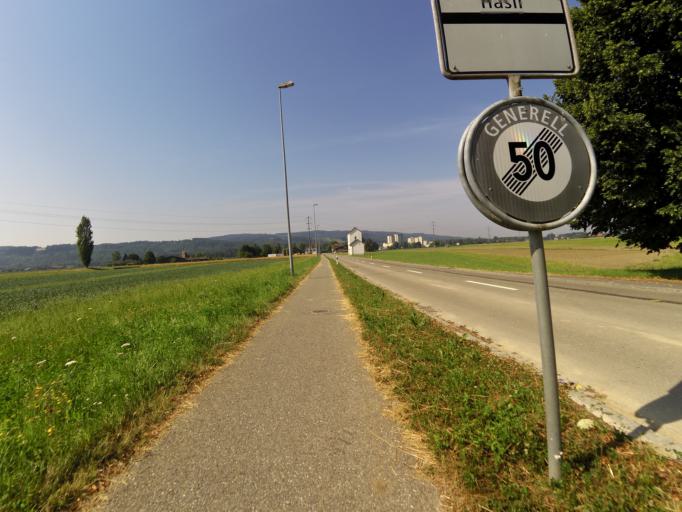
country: CH
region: Thurgau
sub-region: Weinfelden District
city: Wigoltingen
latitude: 47.5954
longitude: 9.0242
